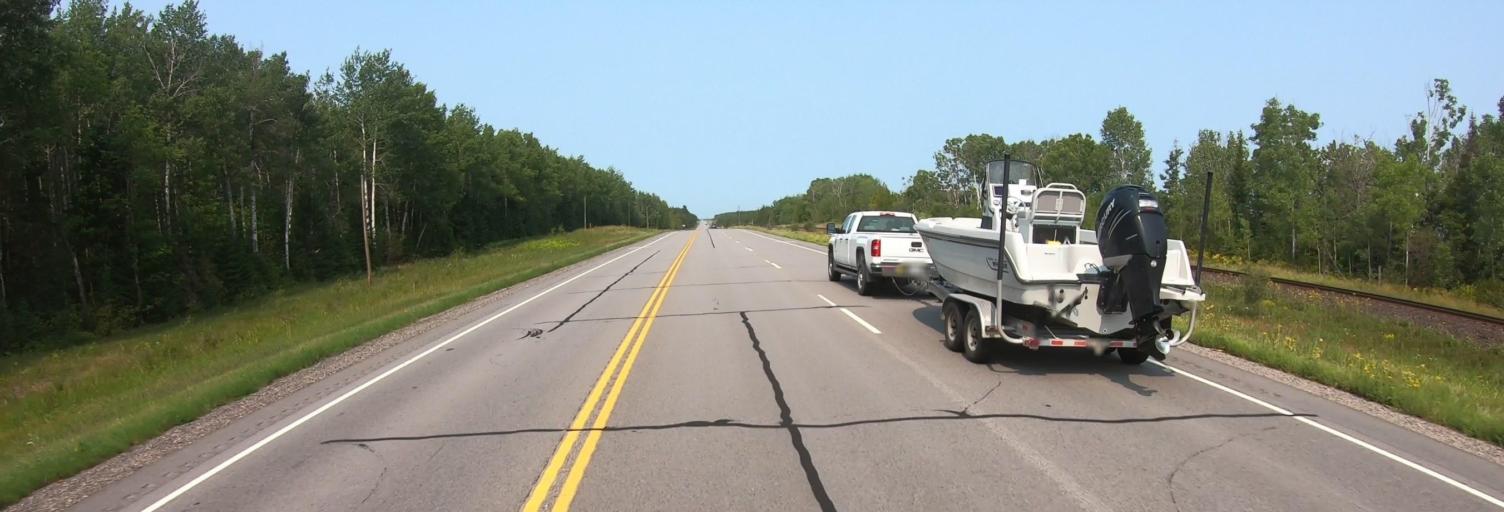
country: CA
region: Ontario
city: Fort Frances
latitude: 48.4497
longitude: -93.2703
